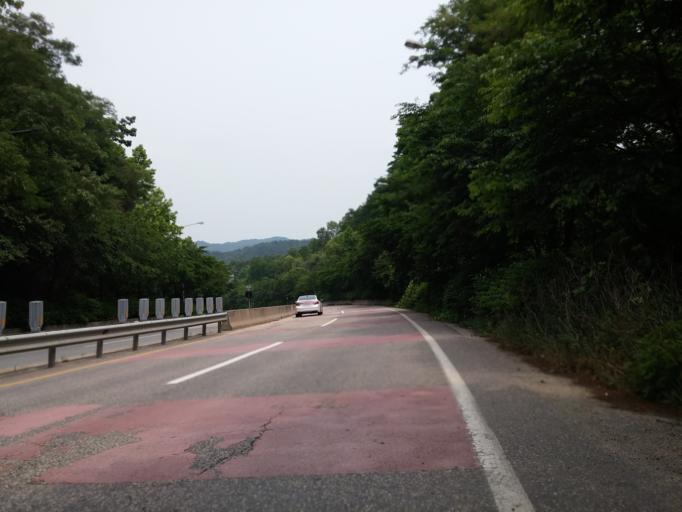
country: KR
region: Daejeon
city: Daejeon
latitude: 36.3475
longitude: 127.4752
